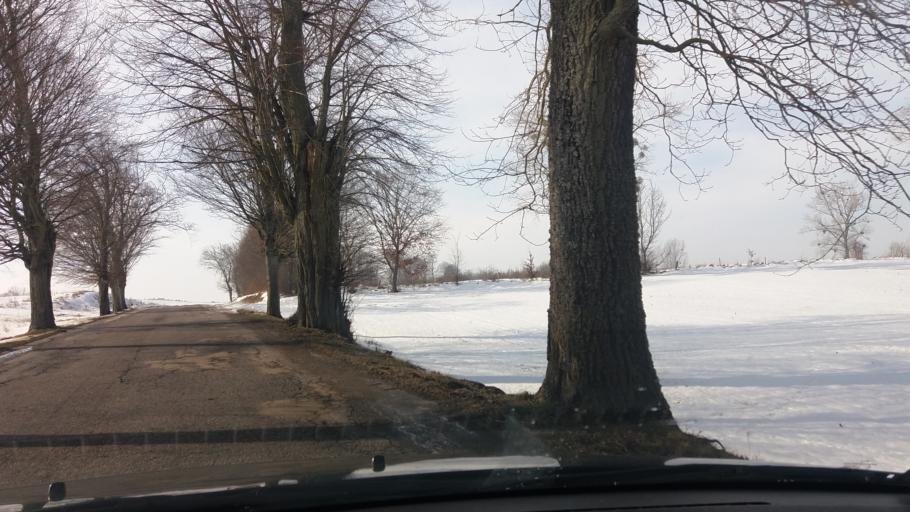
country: PL
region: Warmian-Masurian Voivodeship
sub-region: Powiat olsztynski
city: Jeziorany
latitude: 54.1025
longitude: 20.7281
